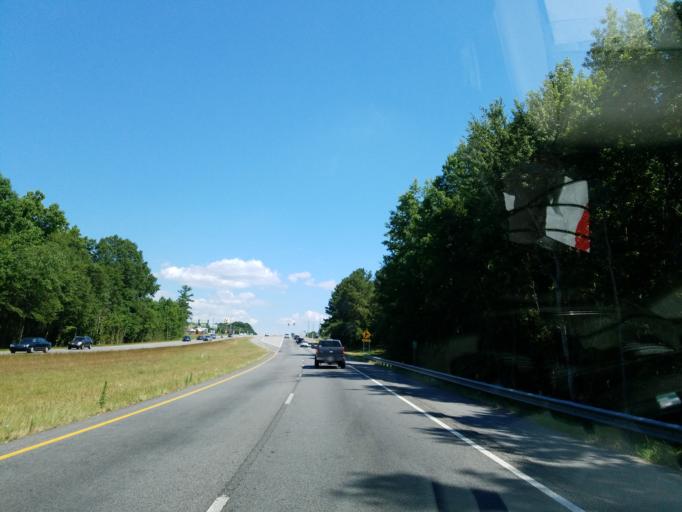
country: US
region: Georgia
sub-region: Spalding County
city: Griffin
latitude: 33.2011
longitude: -84.2877
